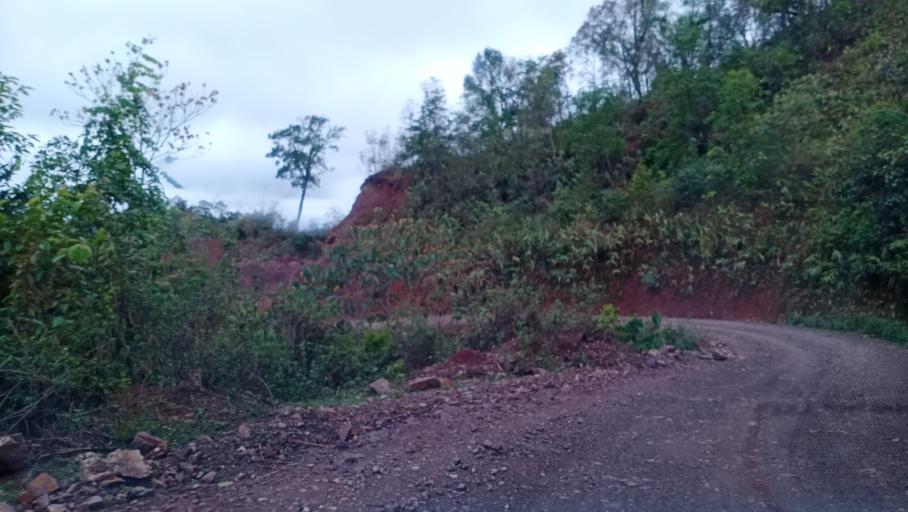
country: LA
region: Phongsali
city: Phongsali
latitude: 21.3391
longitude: 102.0775
